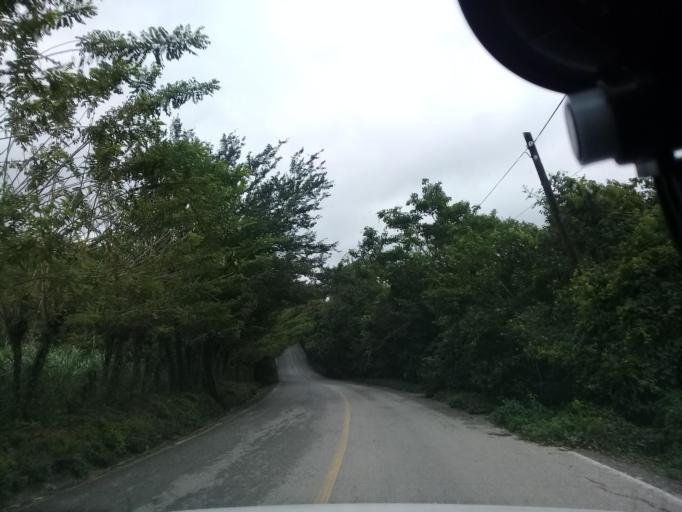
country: MX
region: Veracruz
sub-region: Chalma
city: San Pedro Coyutla
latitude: 21.2083
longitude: -98.4200
